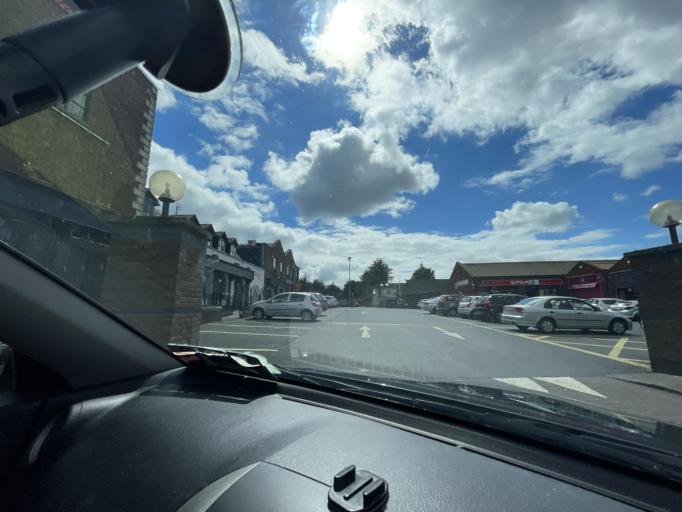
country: IE
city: Cherry Orchard
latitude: 53.3237
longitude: -6.3792
